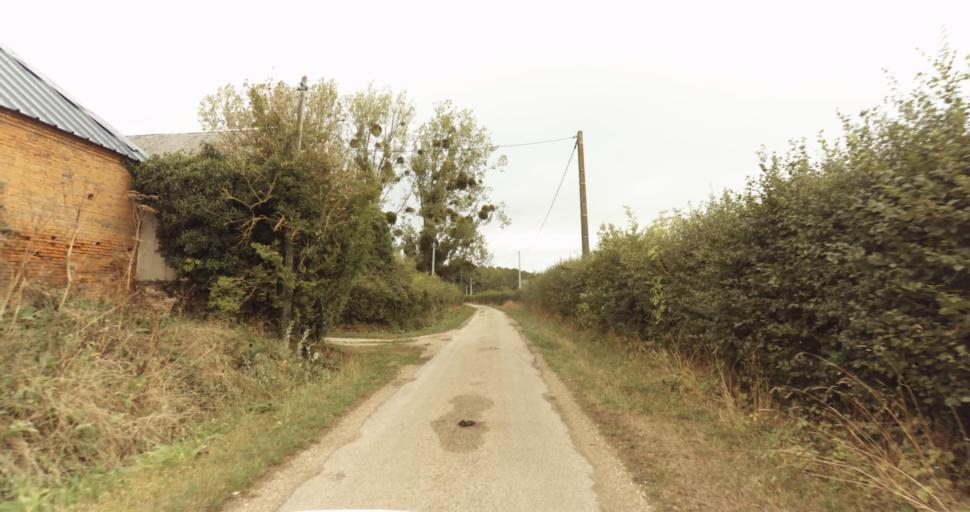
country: FR
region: Lower Normandy
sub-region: Departement de l'Orne
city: Trun
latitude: 48.9196
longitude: 0.0832
